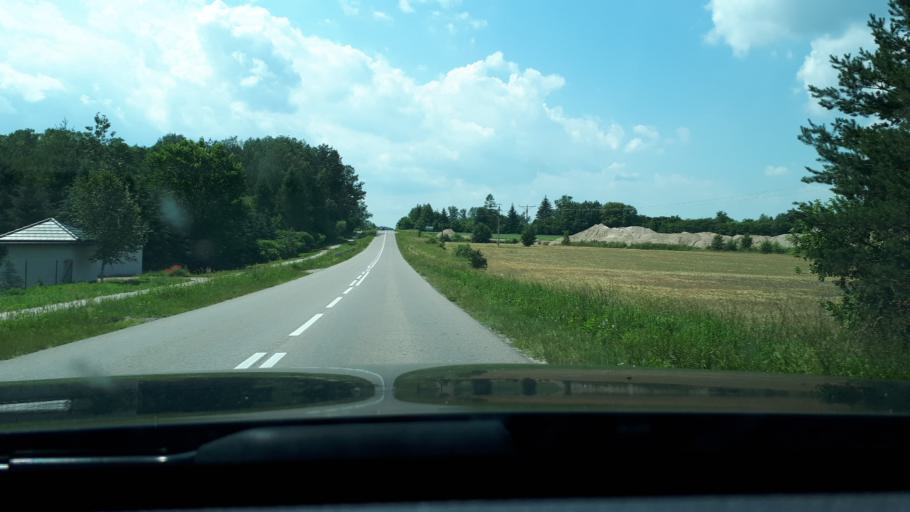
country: PL
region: Podlasie
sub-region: Powiat bialostocki
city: Choroszcz
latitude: 53.1269
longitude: 22.9866
